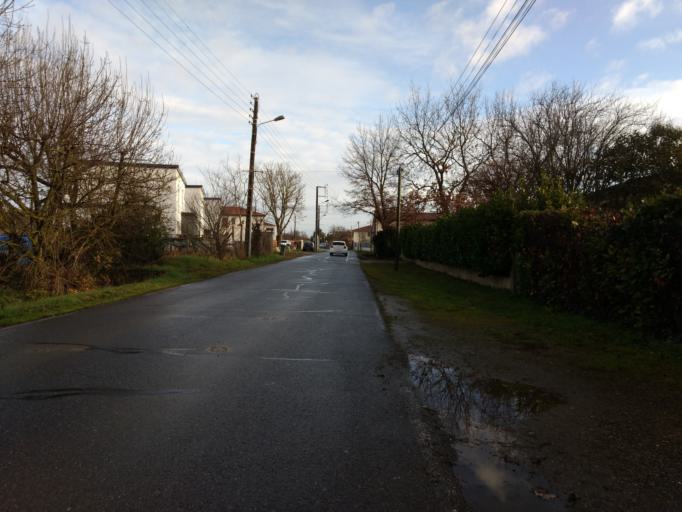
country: FR
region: Midi-Pyrenees
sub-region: Departement de la Haute-Garonne
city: Colomiers
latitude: 43.6082
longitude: 1.3155
